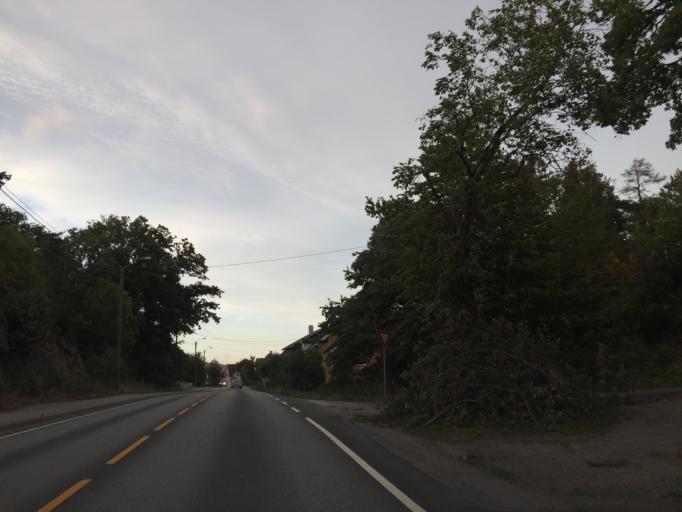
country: NO
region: Ostfold
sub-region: Fredrikstad
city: Fredrikstad
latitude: 59.1934
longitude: 10.9402
